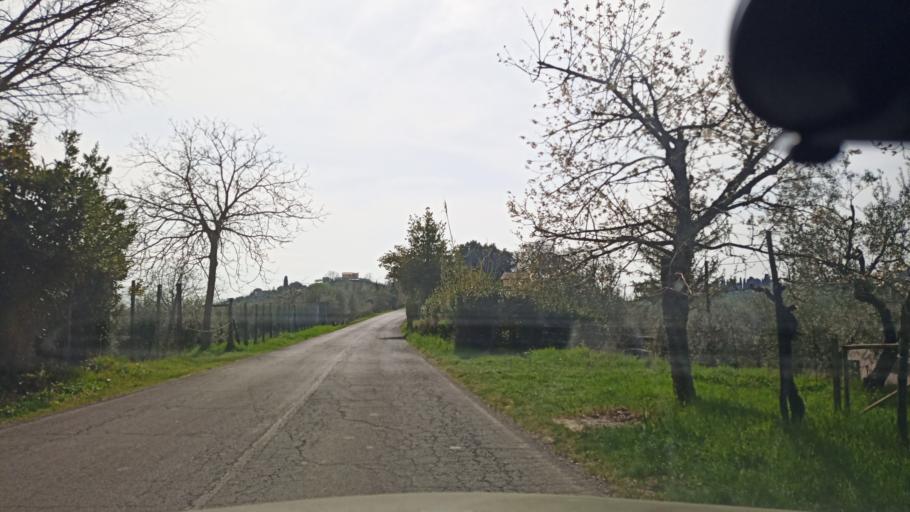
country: IT
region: Latium
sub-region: Provincia di Rieti
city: Torri in Sabina
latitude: 42.3599
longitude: 12.6519
